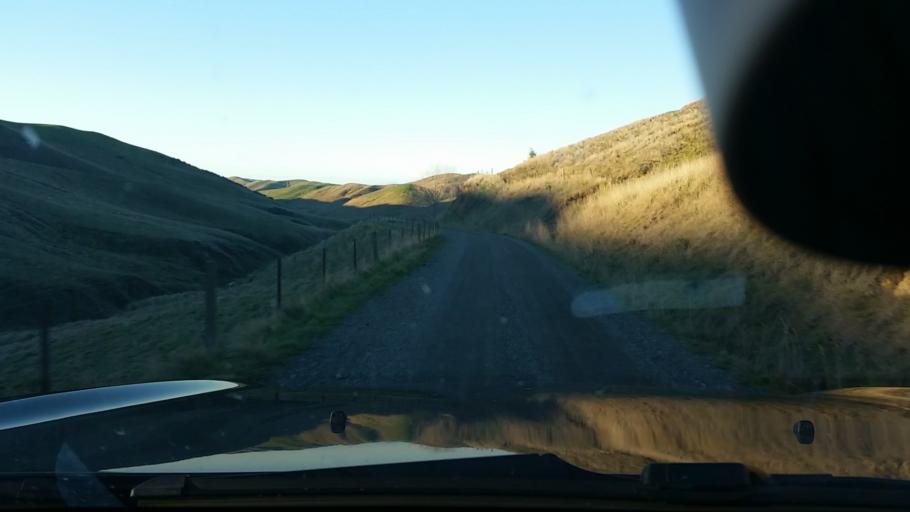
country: NZ
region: Marlborough
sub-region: Marlborough District
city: Blenheim
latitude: -41.7488
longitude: 174.0613
